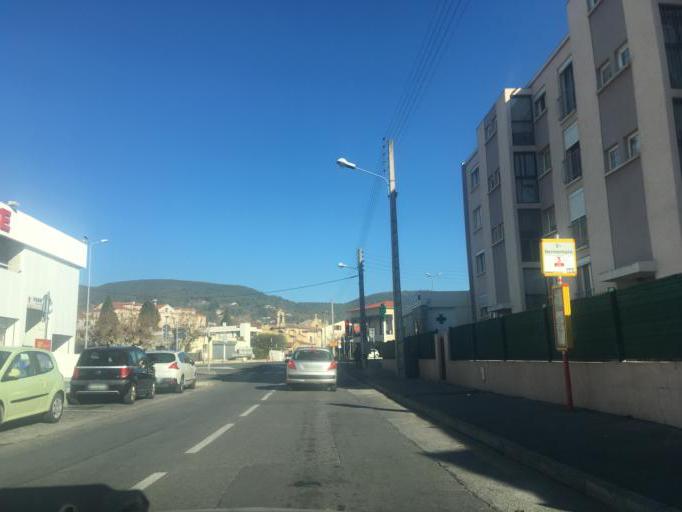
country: FR
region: Provence-Alpes-Cote d'Azur
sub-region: Departement du Var
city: Draguignan
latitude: 43.5336
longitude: 6.4577
